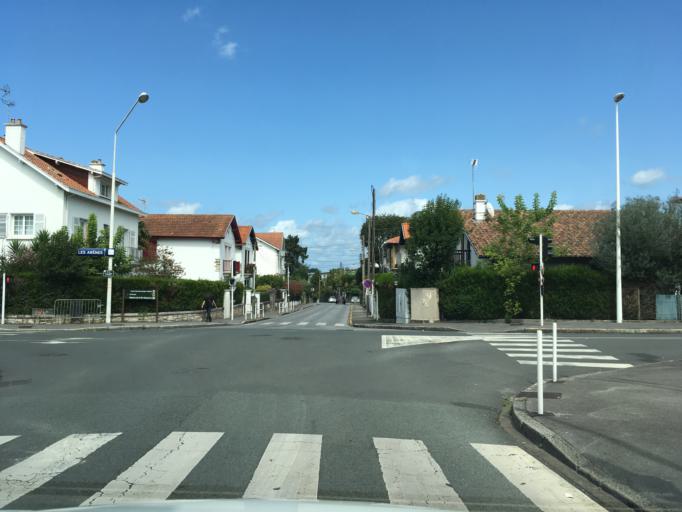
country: FR
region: Aquitaine
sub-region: Departement des Pyrenees-Atlantiques
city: Bayonne
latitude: 43.4922
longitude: -1.4869
